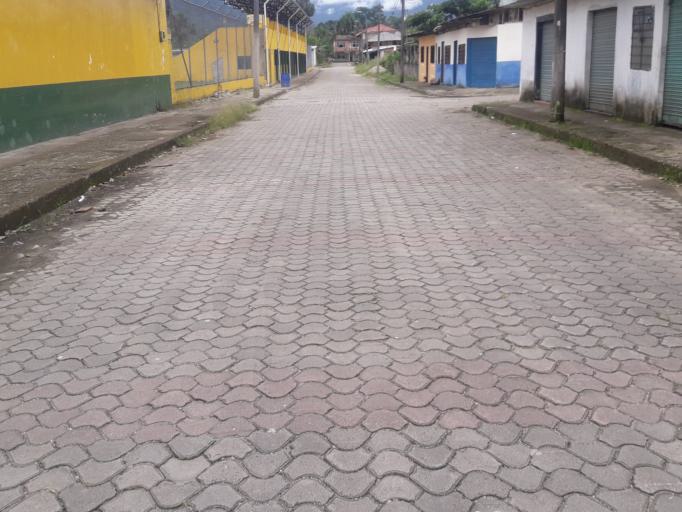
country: EC
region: Napo
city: Tena
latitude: -0.9860
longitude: -77.8283
